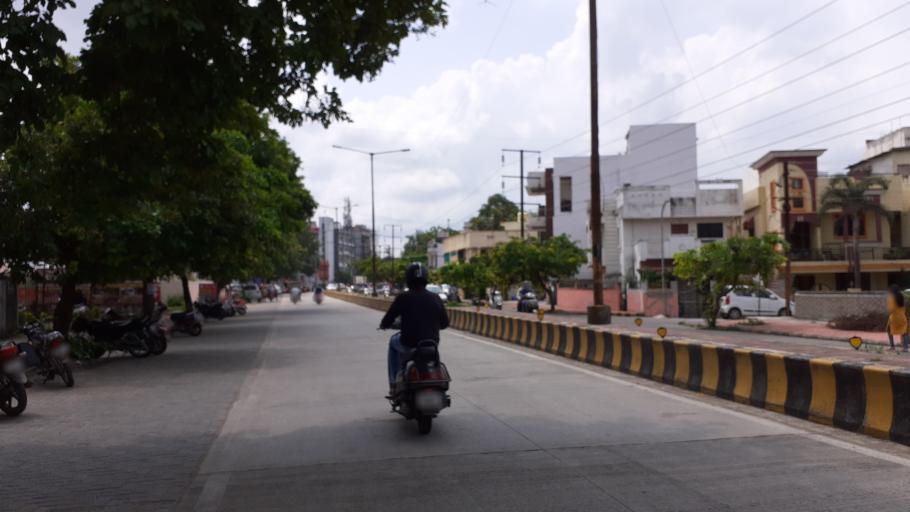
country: IN
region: Maharashtra
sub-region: Nagpur Division
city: Nagpur
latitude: 21.1260
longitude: 79.1187
